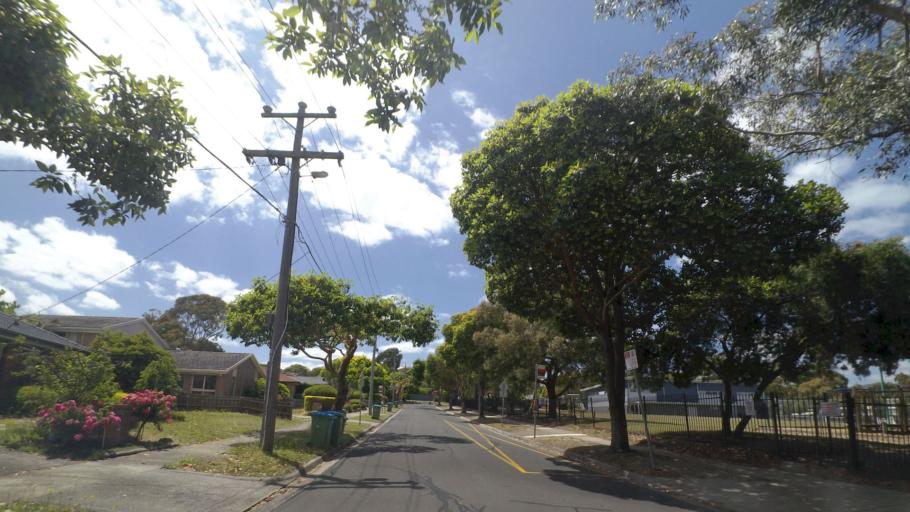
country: AU
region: Victoria
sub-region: Maroondah
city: Bayswater North
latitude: -37.8275
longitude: 145.2947
